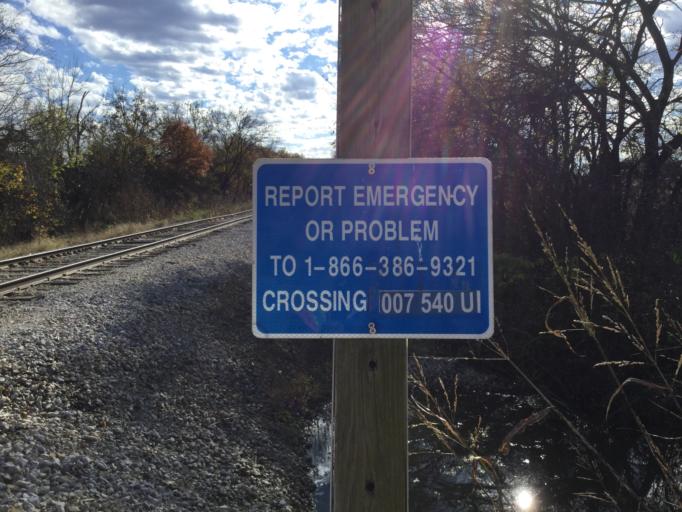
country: US
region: Kansas
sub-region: Montgomery County
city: Cherryvale
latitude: 37.1800
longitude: -95.5808
